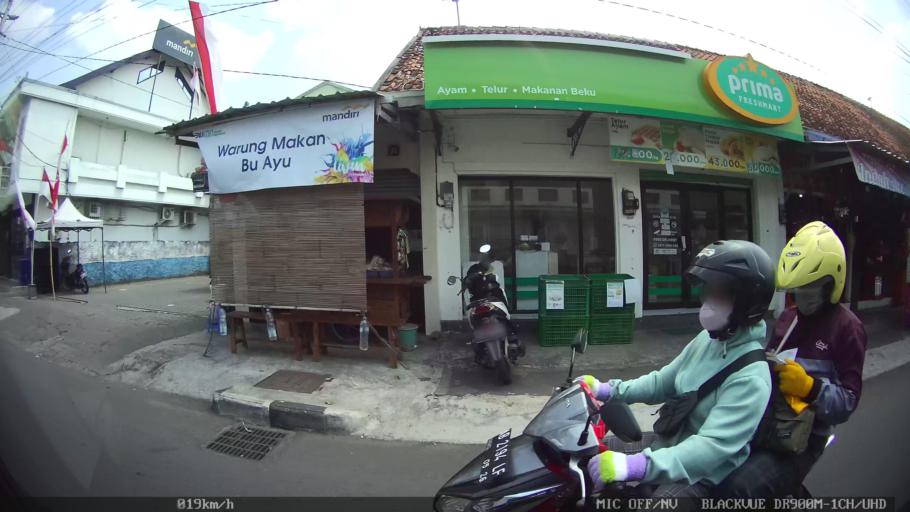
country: ID
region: Daerah Istimewa Yogyakarta
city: Yogyakarta
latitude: -7.8246
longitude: 110.4004
